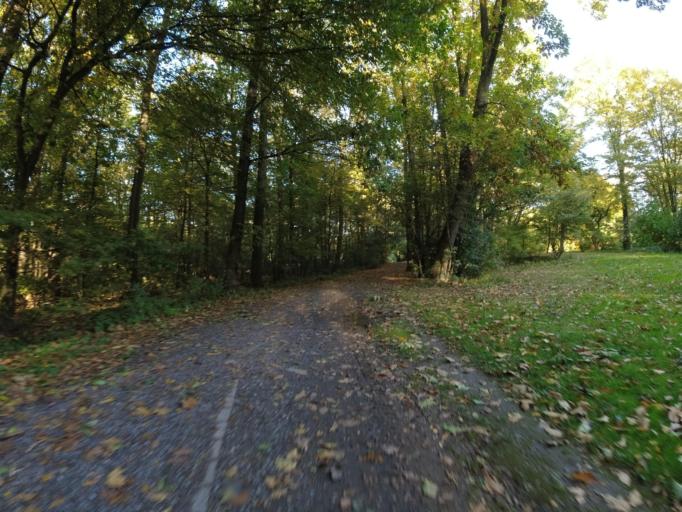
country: DE
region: North Rhine-Westphalia
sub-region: Regierungsbezirk Dusseldorf
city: Hochfeld
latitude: 51.4100
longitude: 6.7037
